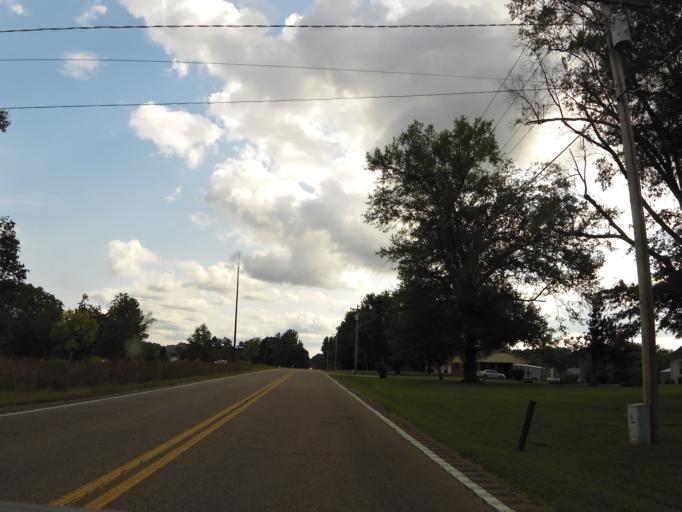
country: US
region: Mississippi
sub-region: Alcorn County
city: Farmington
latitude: 35.0204
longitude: -88.4553
